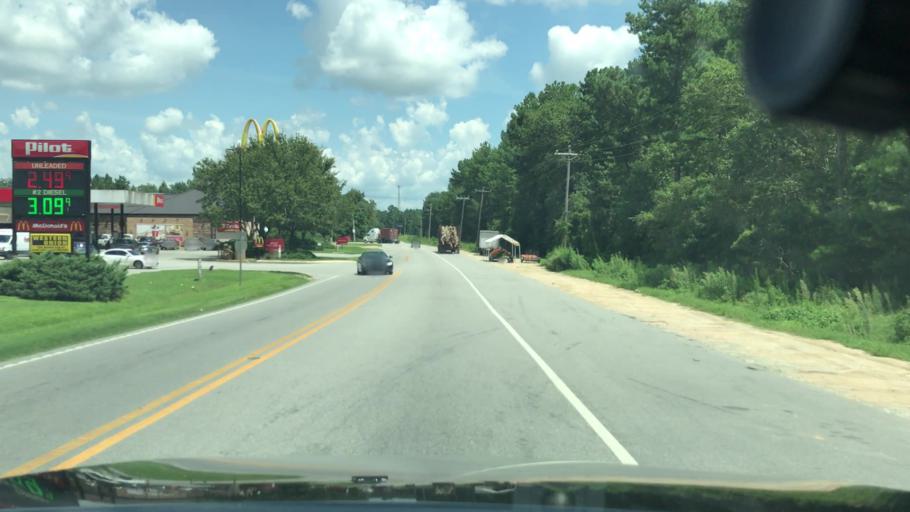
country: US
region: South Carolina
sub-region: Orangeburg County
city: Brookdale
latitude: 33.4158
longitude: -80.6665
